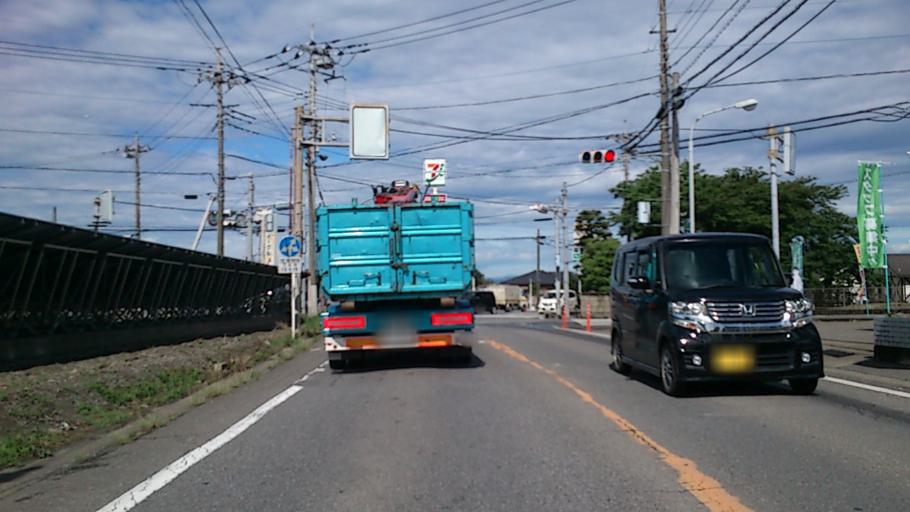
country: JP
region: Gunma
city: Fujioka
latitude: 36.2631
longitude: 139.0585
